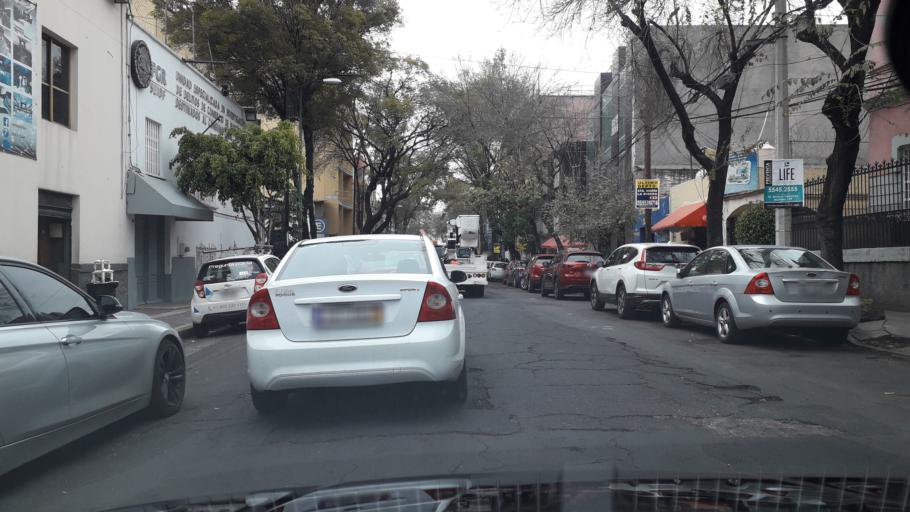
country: MX
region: Mexico City
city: Cuauhtemoc
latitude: 19.4455
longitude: -99.1558
